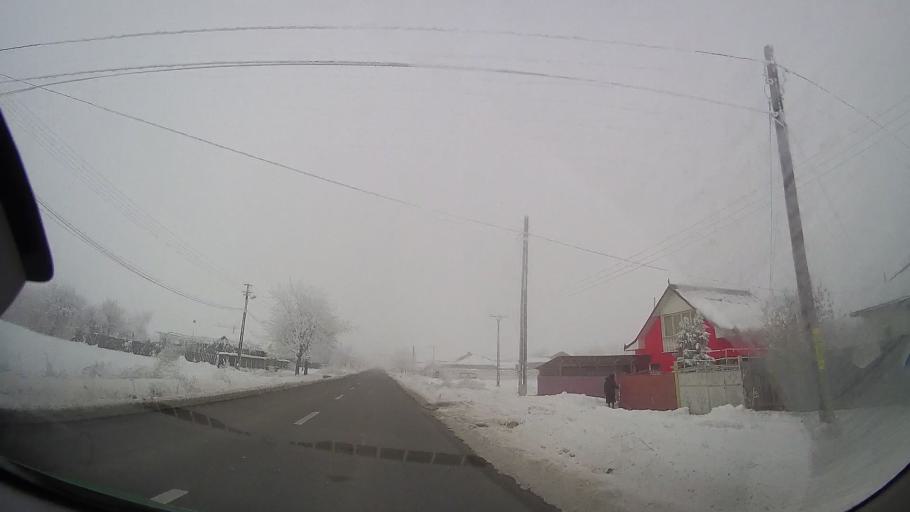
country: RO
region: Iasi
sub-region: Comuna Mogosesti-Siret
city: Mogosesti-Siret
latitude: 47.1389
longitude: 26.7802
